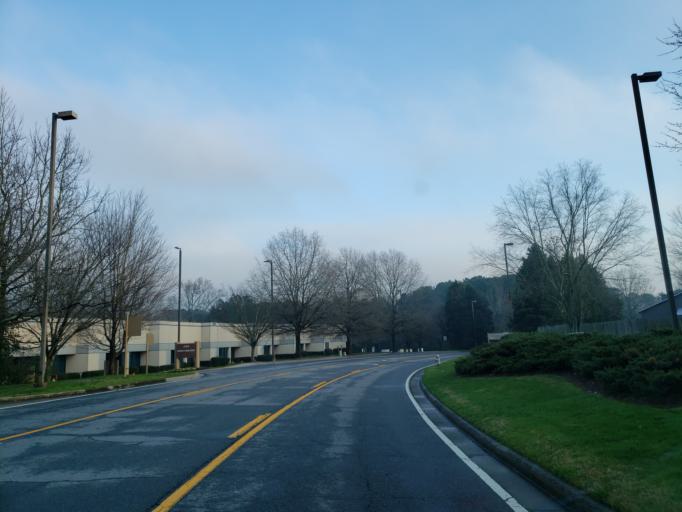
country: US
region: Georgia
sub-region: Cobb County
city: Kennesaw
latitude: 34.0056
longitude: -84.5944
